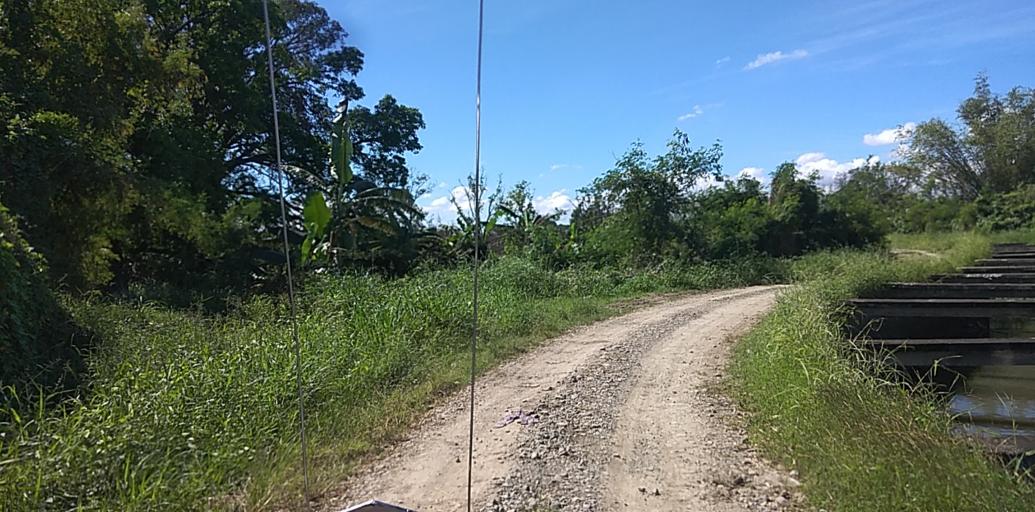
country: PH
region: Central Luzon
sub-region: Province of Pampanga
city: Candating
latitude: 15.1302
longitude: 120.7946
